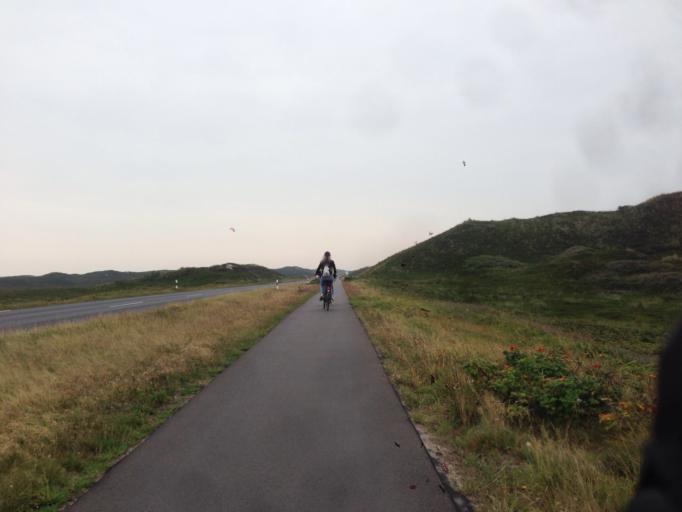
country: DE
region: Schleswig-Holstein
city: Westerland
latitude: 54.7946
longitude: 8.2881
